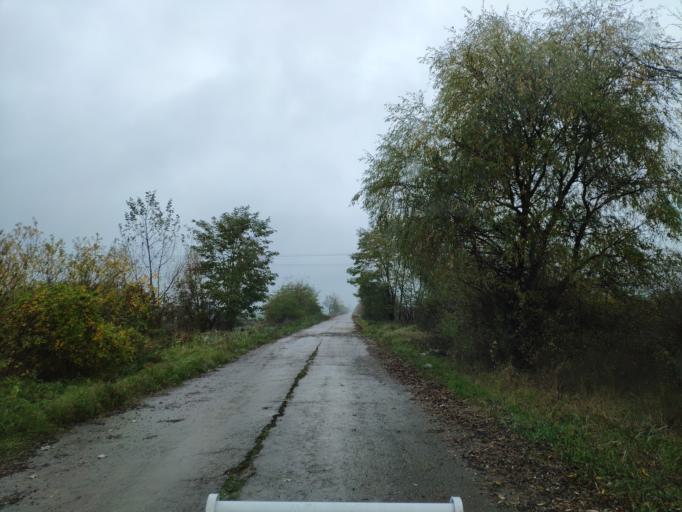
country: SK
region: Kosicky
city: Cierna nad Tisou
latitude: 48.4275
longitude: 22.0032
